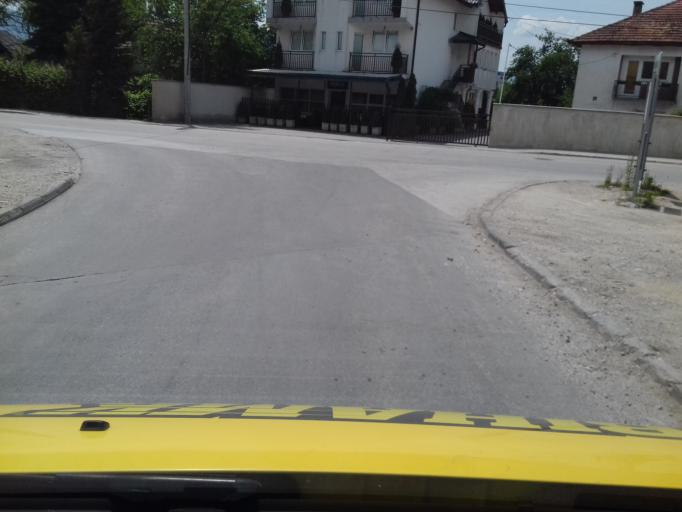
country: BA
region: Federation of Bosnia and Herzegovina
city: Vogosca
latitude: 43.8760
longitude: 18.3093
